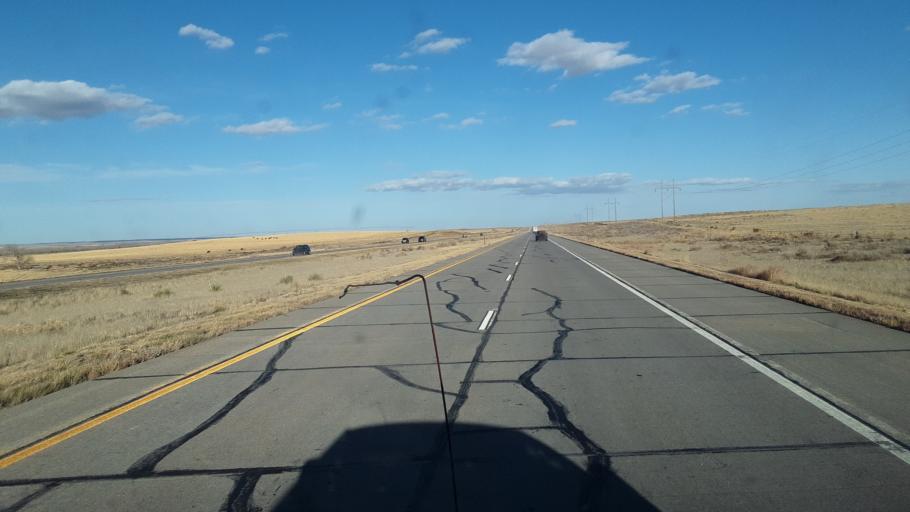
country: US
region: Colorado
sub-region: Logan County
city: Sterling
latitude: 40.7871
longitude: -102.8972
